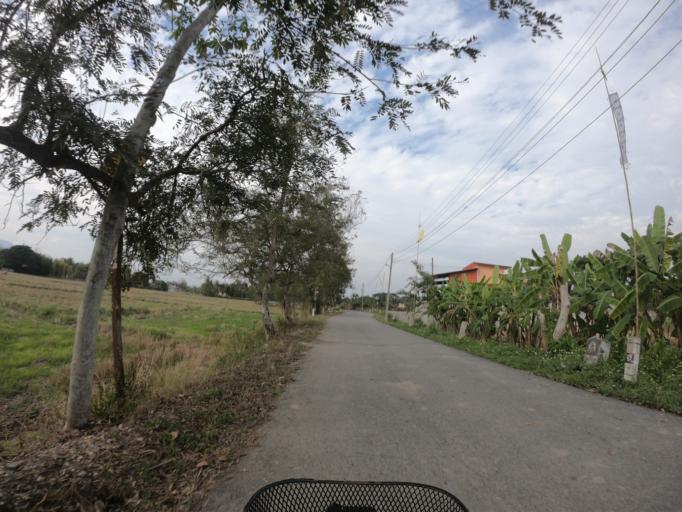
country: TH
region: Chiang Mai
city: San Sai
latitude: 18.7971
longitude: 99.0531
